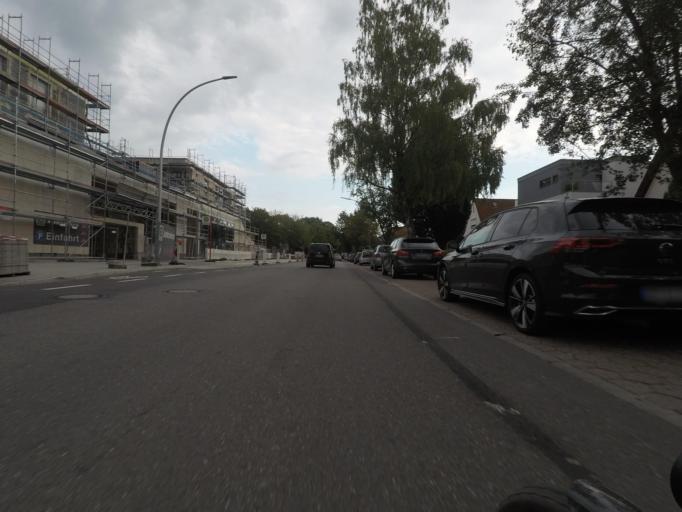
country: DE
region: Hamburg
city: Farmsen-Berne
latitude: 53.6273
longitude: 10.1678
